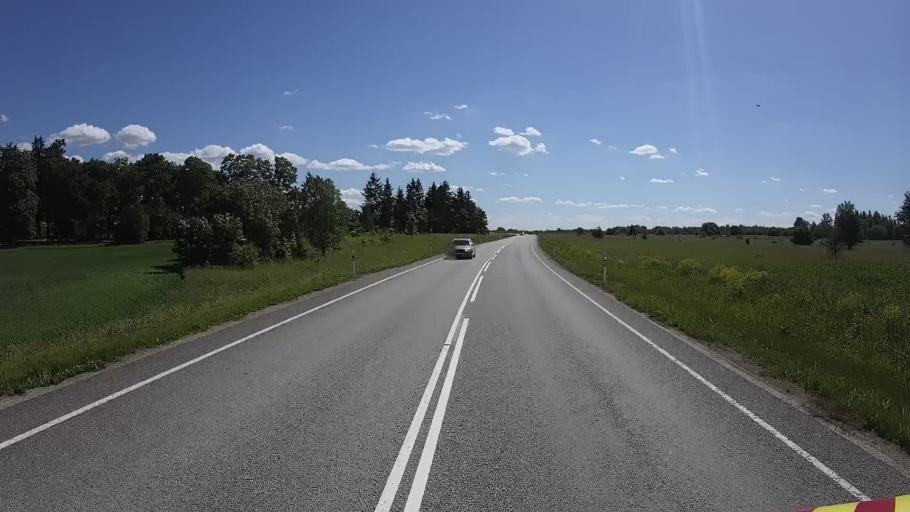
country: EE
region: Ida-Virumaa
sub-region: Johvi vald
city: Johvi
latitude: 59.3778
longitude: 27.3511
